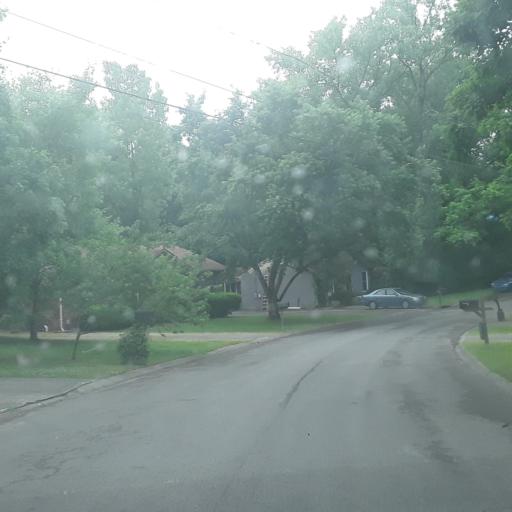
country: US
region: Tennessee
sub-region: Williamson County
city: Brentwood
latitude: 36.0583
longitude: -86.7301
